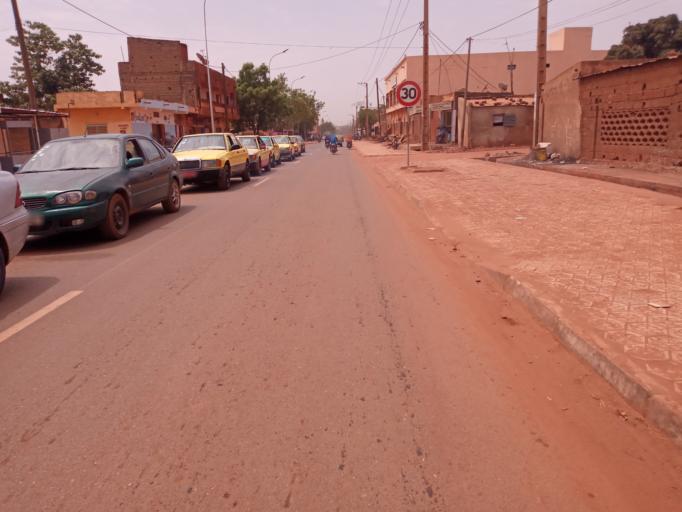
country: ML
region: Bamako
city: Bamako
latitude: 12.5883
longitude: -7.9883
